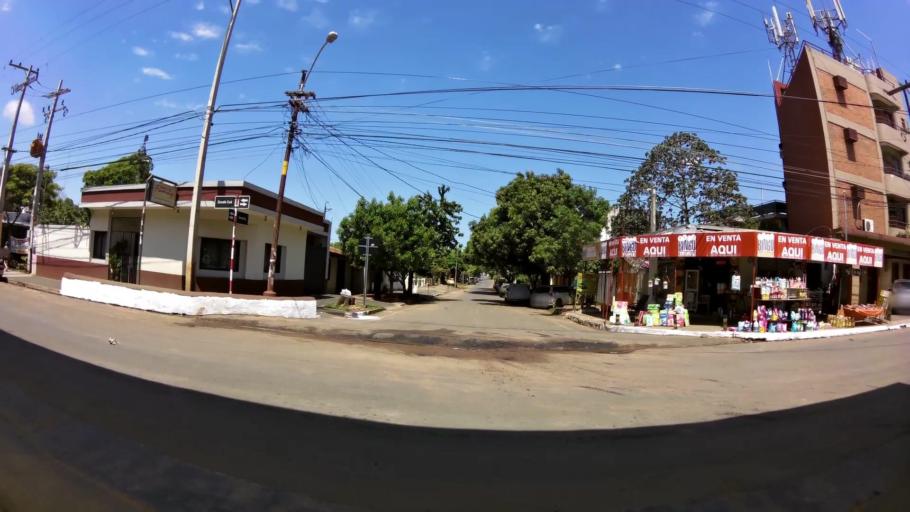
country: PY
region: Central
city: Fernando de la Mora
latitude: -25.3260
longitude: -57.5539
